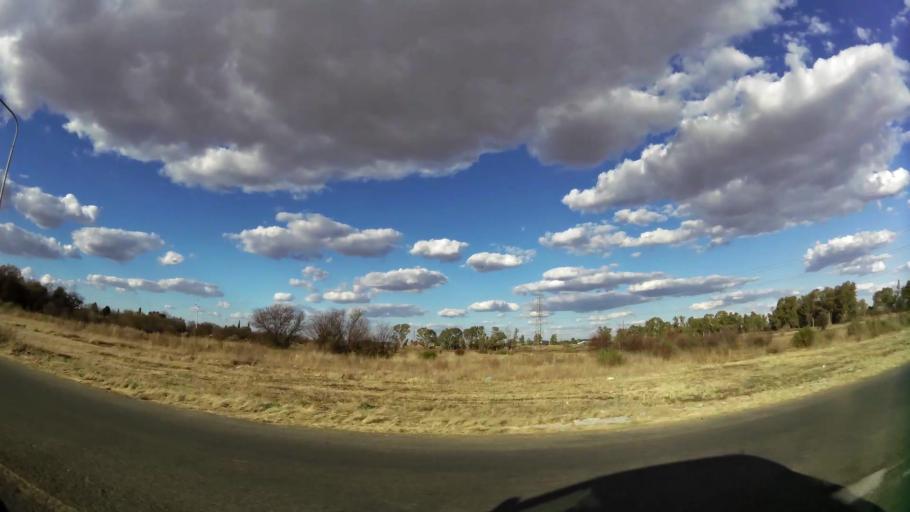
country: ZA
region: North-West
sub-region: Dr Kenneth Kaunda District Municipality
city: Potchefstroom
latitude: -26.7050
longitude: 27.0781
